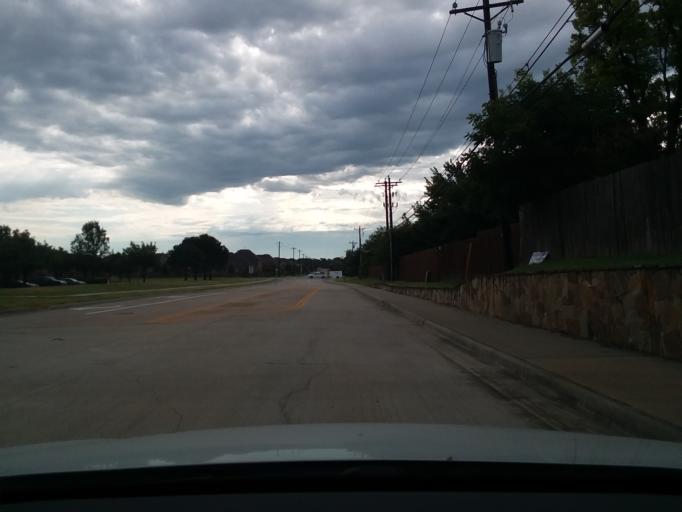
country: US
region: Texas
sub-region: Denton County
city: Highland Village
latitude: 33.0605
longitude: -97.0536
